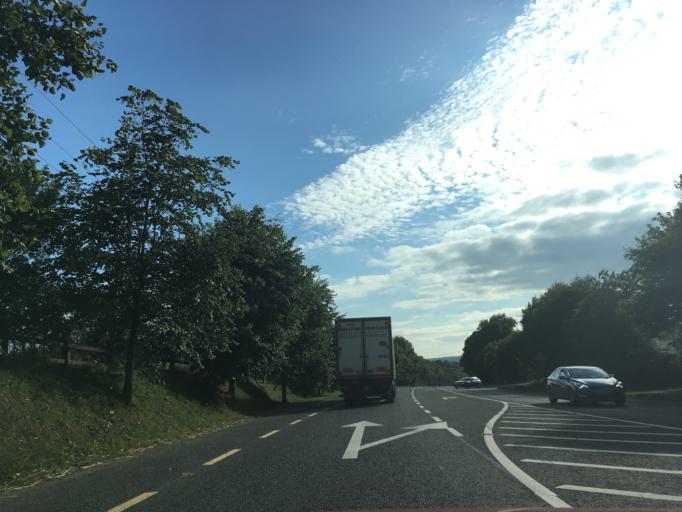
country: IE
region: Leinster
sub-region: Loch Garman
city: New Ross
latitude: 52.3850
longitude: -6.9273
